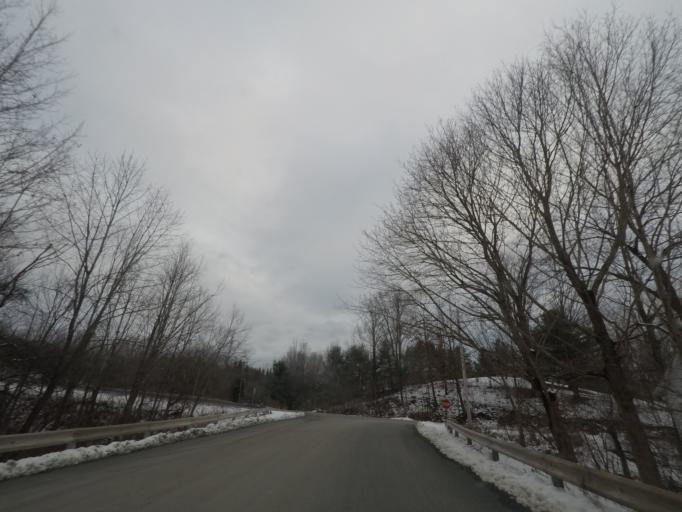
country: US
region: New York
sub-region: Rensselaer County
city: Averill Park
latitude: 42.6388
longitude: -73.5372
